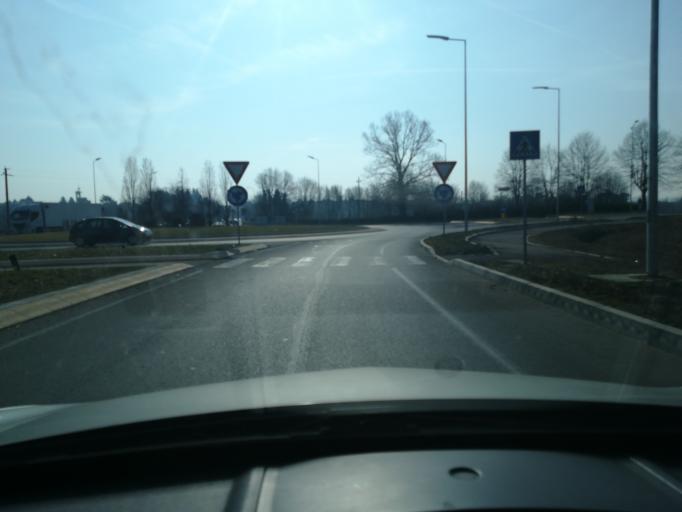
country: IT
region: Lombardy
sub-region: Provincia di Brescia
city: Palazzolo sull'Oglio
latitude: 45.5947
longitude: 9.8727
